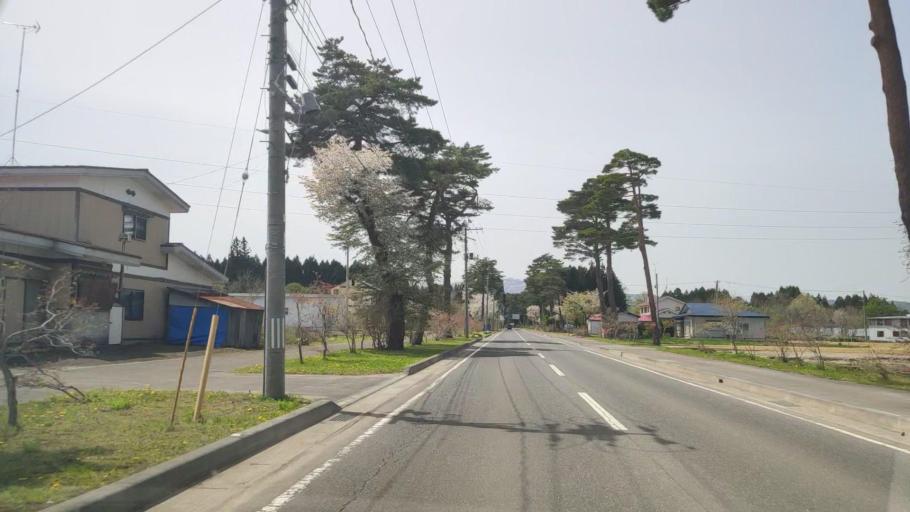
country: JP
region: Aomori
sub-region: Misawa Shi
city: Inuotose
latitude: 40.7157
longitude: 141.1485
